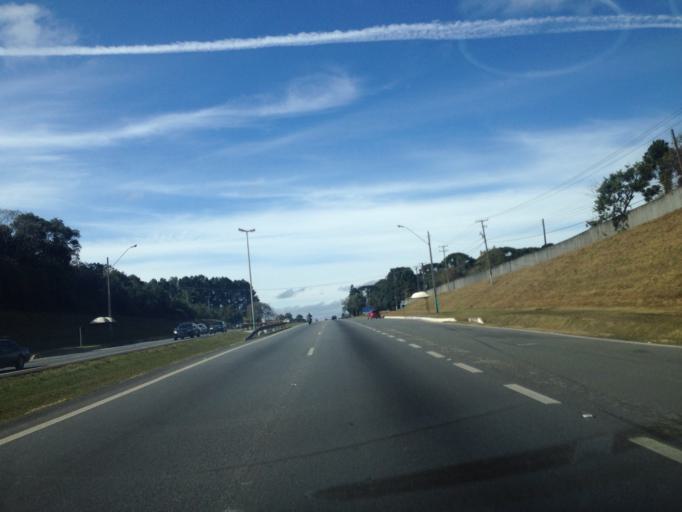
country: BR
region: Parana
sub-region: Sao Jose Dos Pinhais
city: Sao Jose dos Pinhais
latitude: -25.5050
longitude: -49.1428
